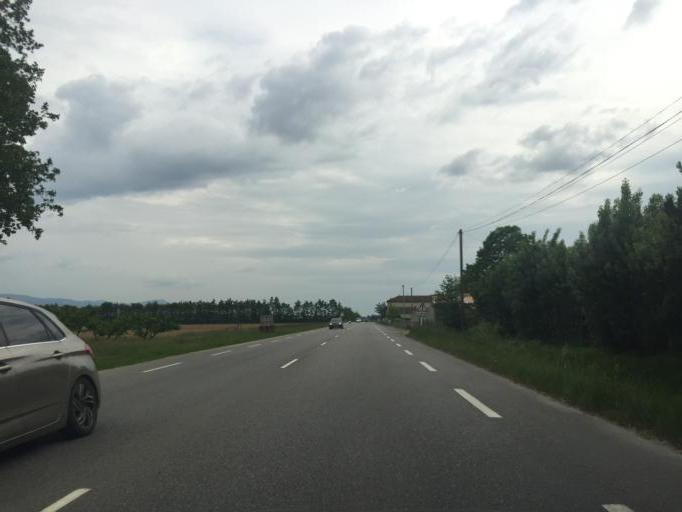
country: FR
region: Rhone-Alpes
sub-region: Departement de la Drome
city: Alixan
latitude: 45.0091
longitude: 5.0376
